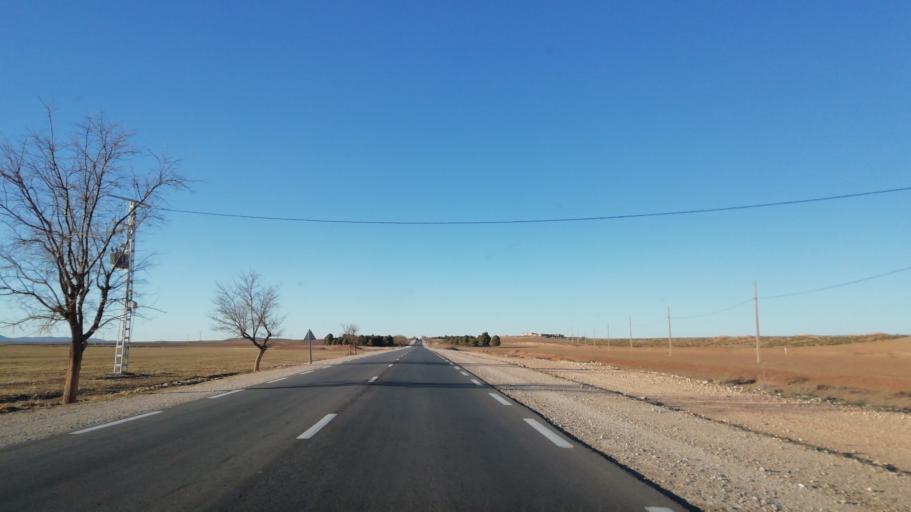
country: DZ
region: Tlemcen
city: Sebdou
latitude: 34.5215
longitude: -1.2896
